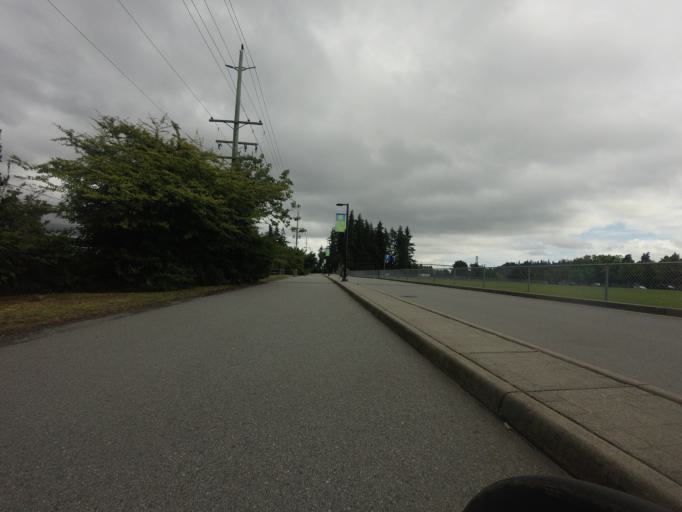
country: CA
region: British Columbia
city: West Vancouver
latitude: 49.3260
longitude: -123.1500
